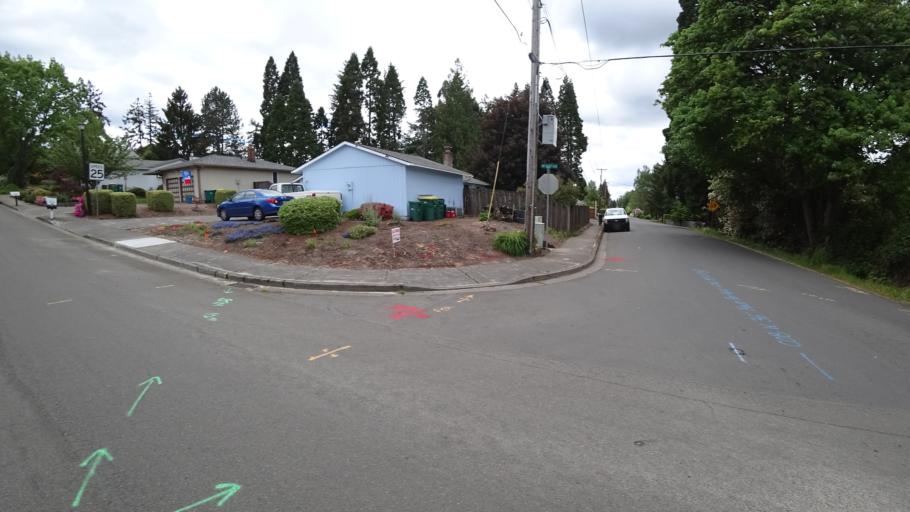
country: US
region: Oregon
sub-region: Washington County
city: Aloha
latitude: 45.4810
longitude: -122.8420
